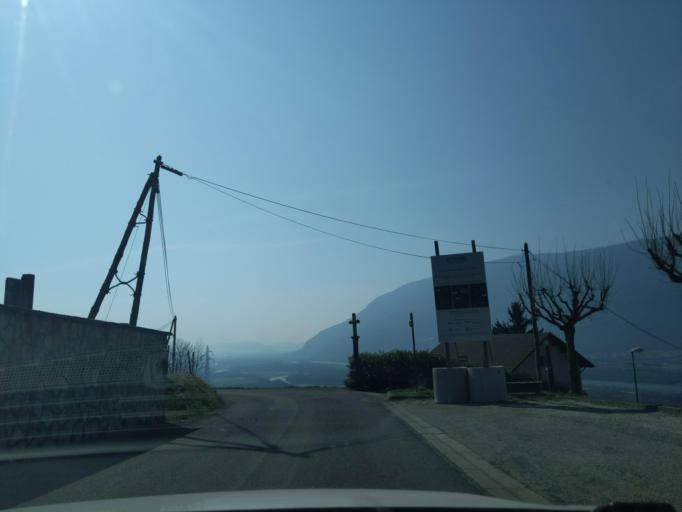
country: FR
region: Rhone-Alpes
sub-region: Departement de la Haute-Savoie
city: Moye
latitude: 45.9177
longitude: 5.8461
